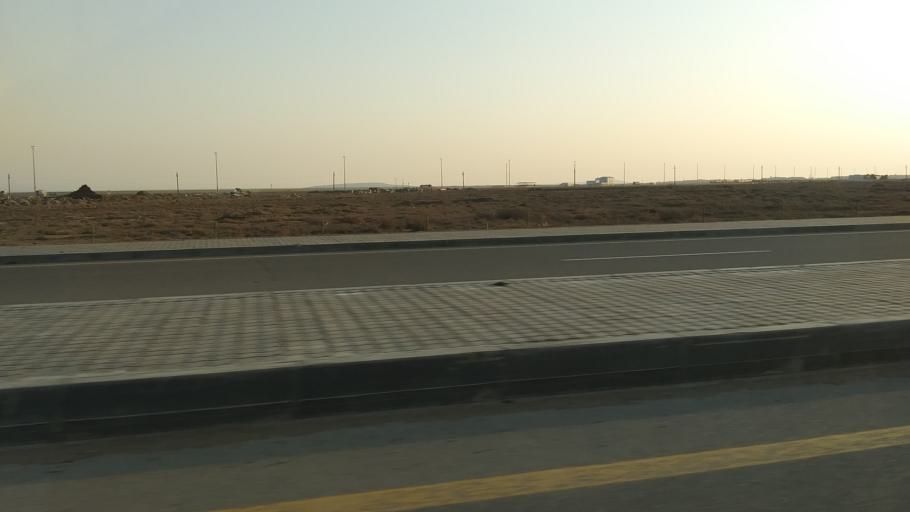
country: AZ
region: Baki
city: Qobustan
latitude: 39.9810
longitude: 49.4353
